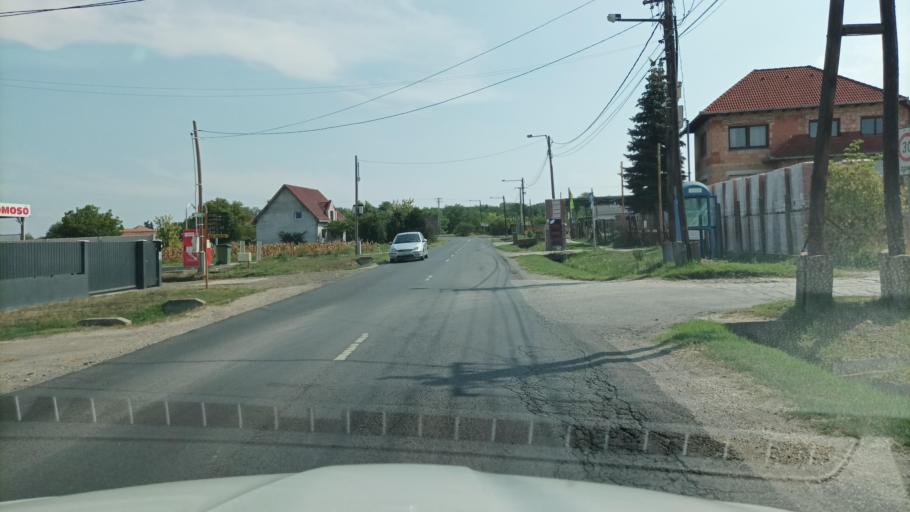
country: HU
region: Pest
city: Hevizgyoerk
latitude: 47.6232
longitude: 19.5338
